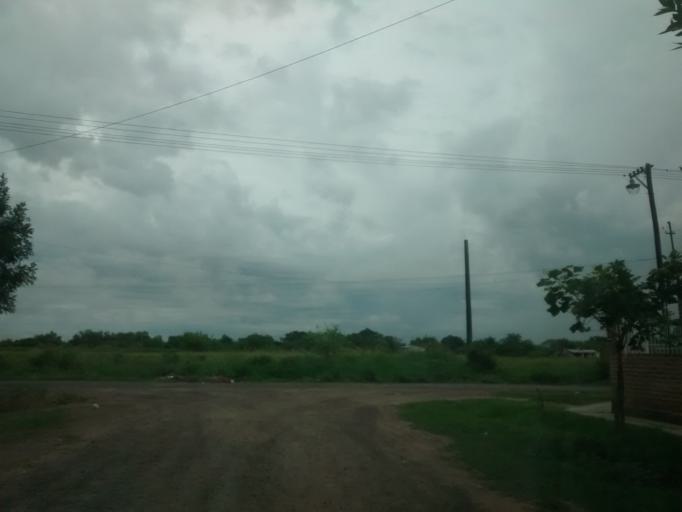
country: AR
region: Chaco
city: Puerto Tirol
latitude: -27.3742
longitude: -59.0989
